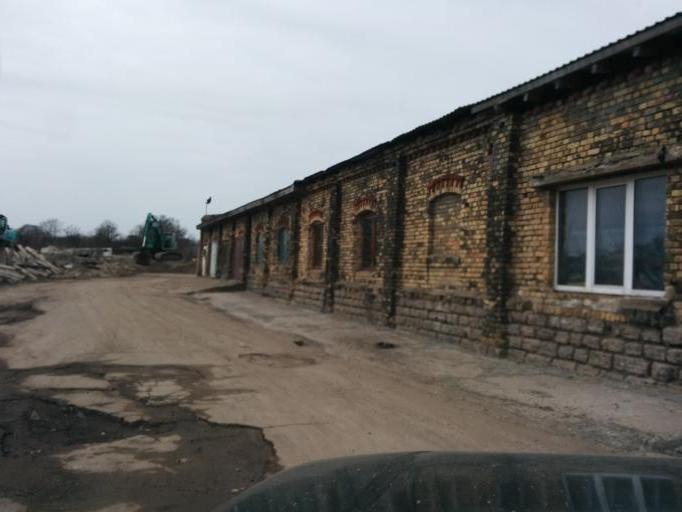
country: LV
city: Tireli
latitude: 56.9448
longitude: 23.6354
